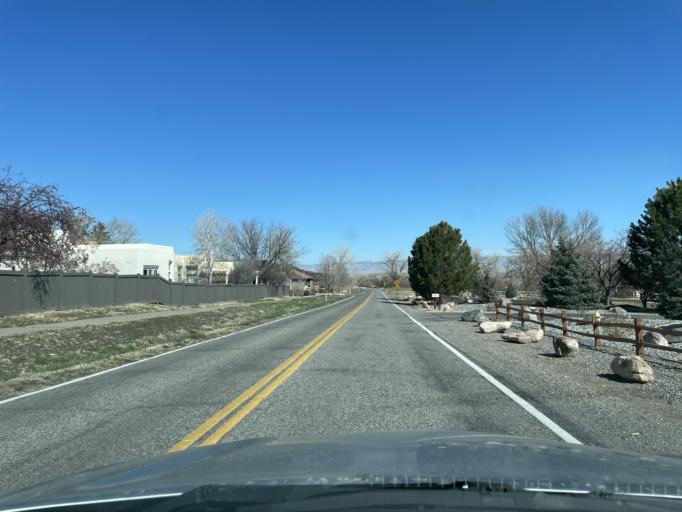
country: US
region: Colorado
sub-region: Mesa County
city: Redlands
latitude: 39.0752
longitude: -108.6640
